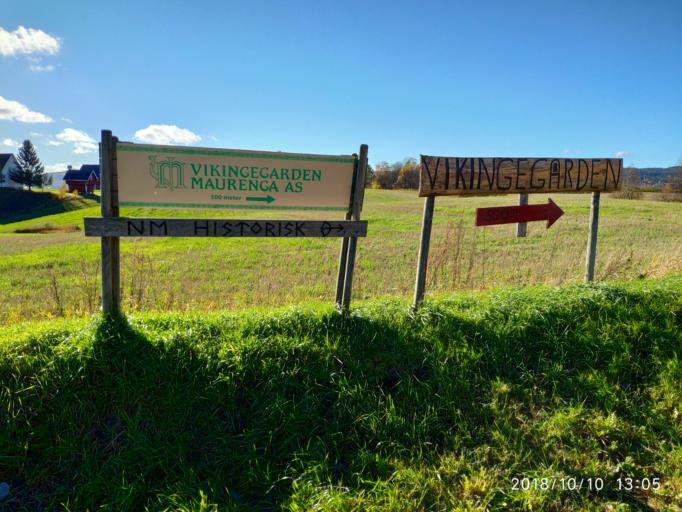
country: NO
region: Akershus
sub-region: Nannestad
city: Teigebyen
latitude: 60.1941
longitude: 11.0306
